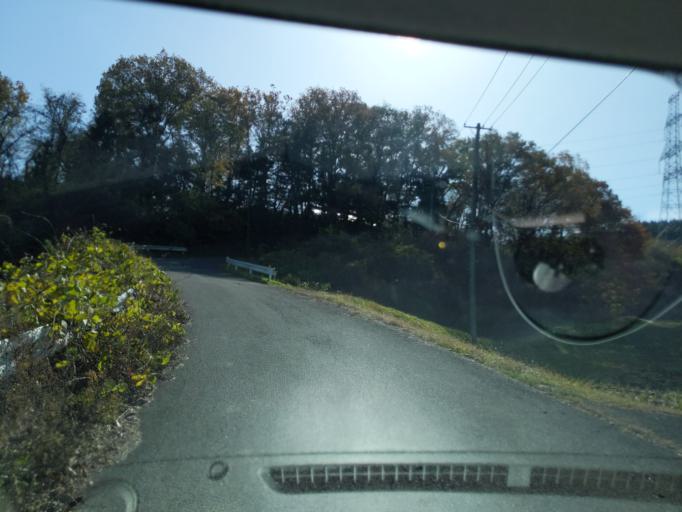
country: JP
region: Iwate
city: Mizusawa
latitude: 39.0282
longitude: 141.1040
